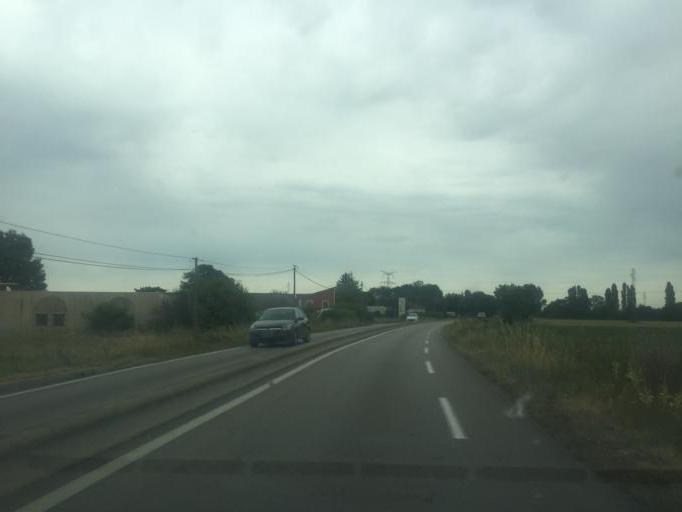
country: FR
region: Rhone-Alpes
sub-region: Departement de l'Ain
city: Beynost
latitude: 45.8288
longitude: 5.0034
